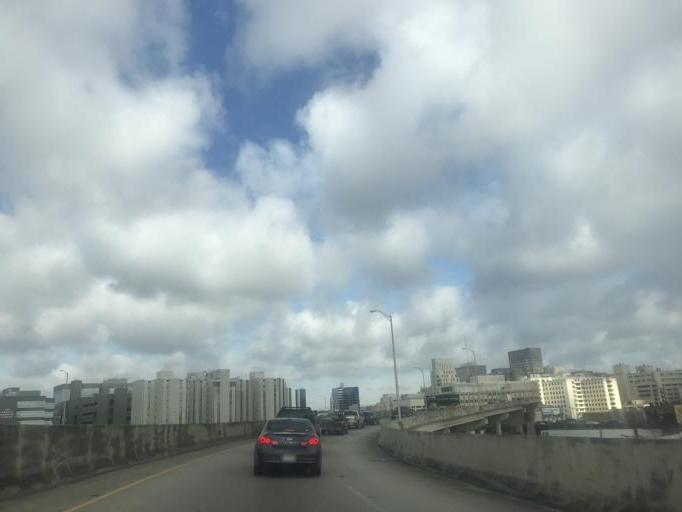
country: US
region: Louisiana
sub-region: Orleans Parish
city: New Orleans
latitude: 29.9531
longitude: -90.0853
